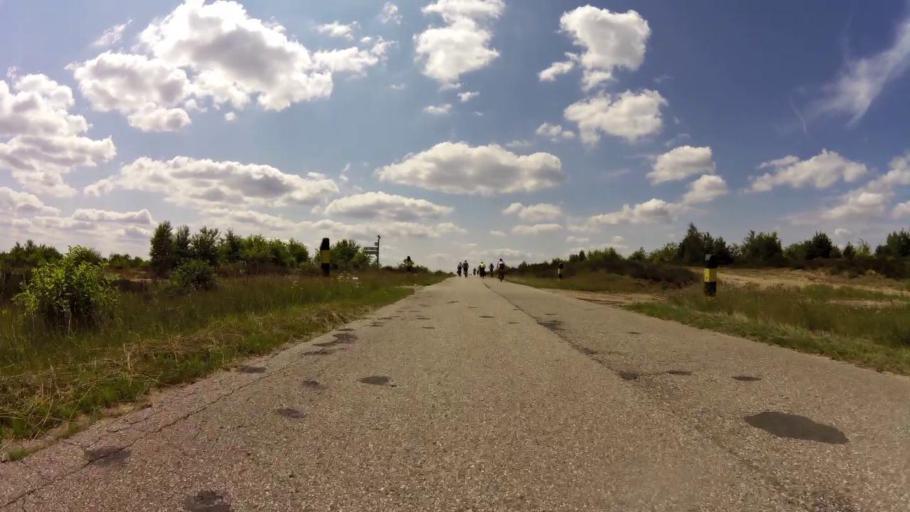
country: PL
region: West Pomeranian Voivodeship
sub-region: Powiat drawski
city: Drawsko Pomorskie
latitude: 53.4348
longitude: 15.7537
